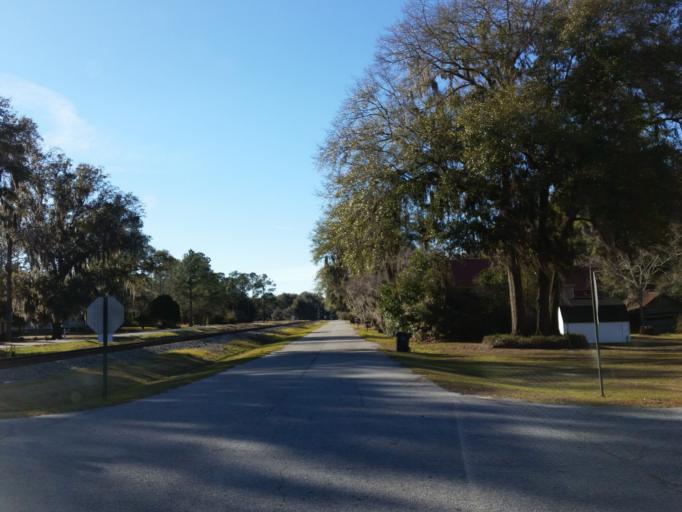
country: US
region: Georgia
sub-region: Echols County
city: Statenville
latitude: 30.6832
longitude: -83.1828
